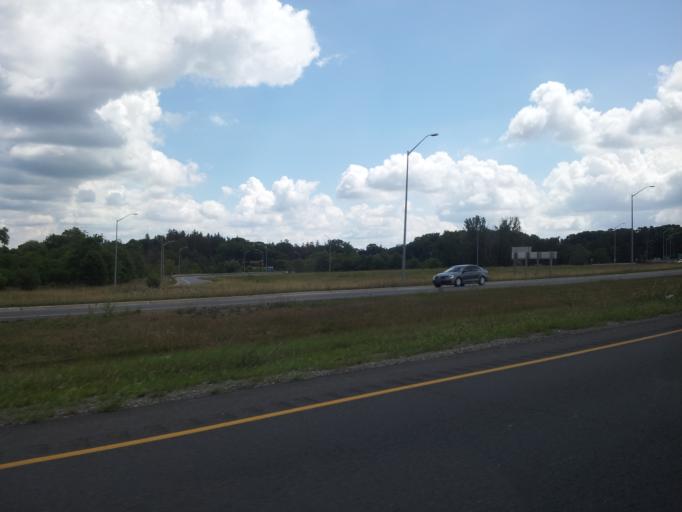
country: CA
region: Ontario
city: Waterloo
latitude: 43.4764
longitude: -80.4964
